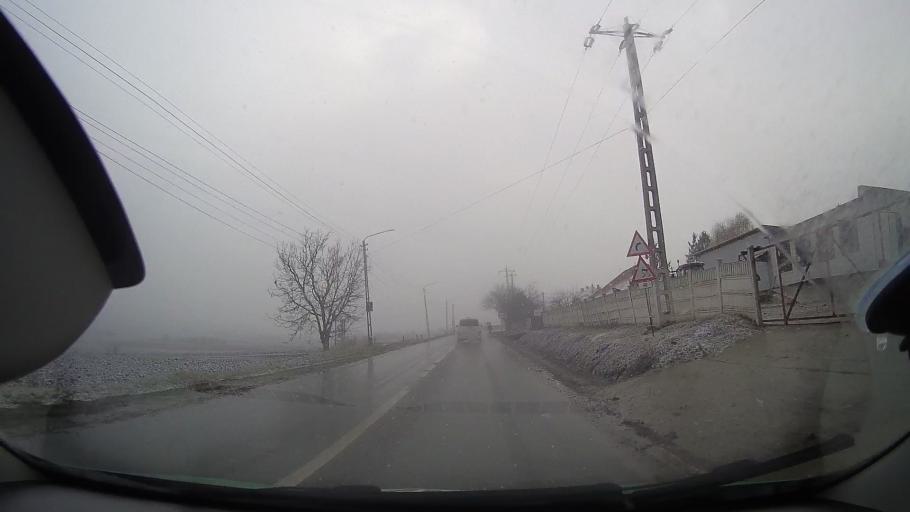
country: RO
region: Mures
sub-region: Municipiul Tarnaveni
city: Tarnaveni
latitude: 46.2885
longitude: 24.3018
